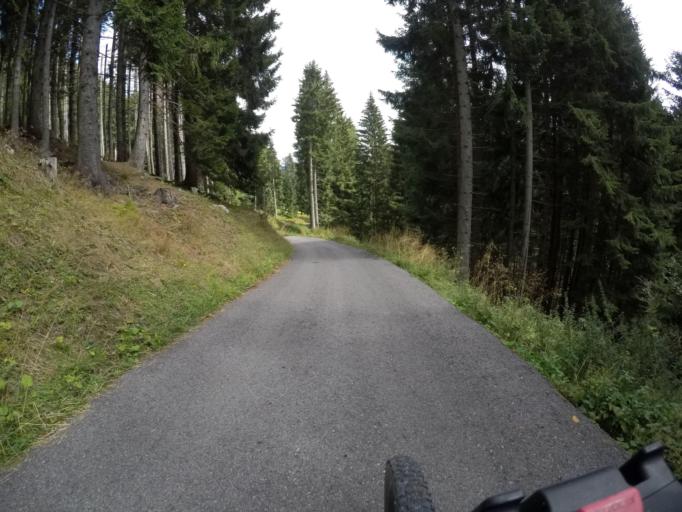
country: IT
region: Friuli Venezia Giulia
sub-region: Provincia di Udine
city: Pontebba
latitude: 46.5138
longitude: 13.2488
